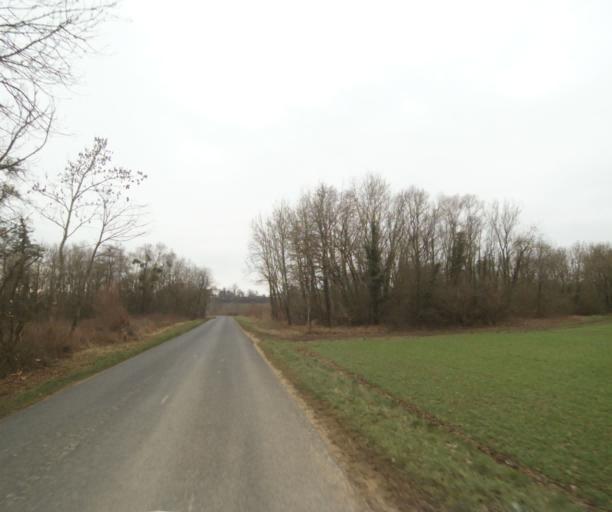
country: FR
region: Champagne-Ardenne
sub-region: Departement de la Haute-Marne
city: Villiers-en-Lieu
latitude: 48.6407
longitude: 4.8383
